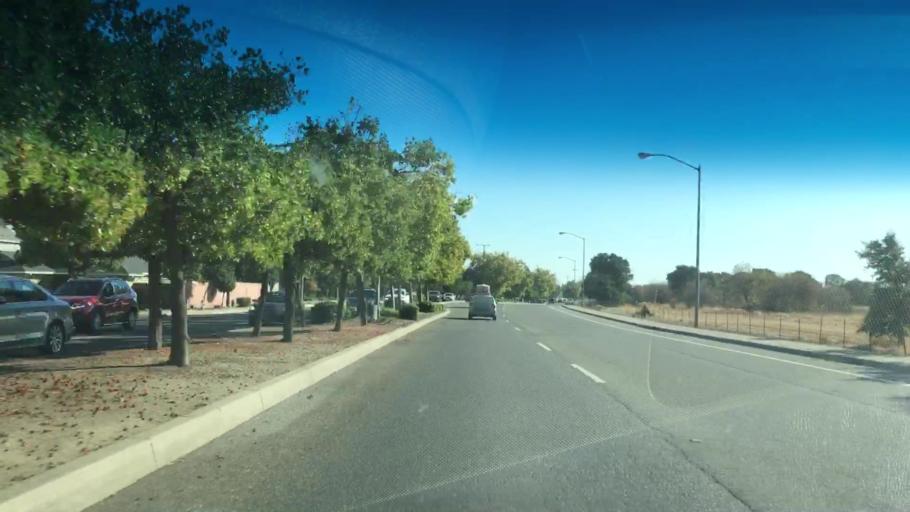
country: US
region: California
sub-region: Sacramento County
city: Laguna
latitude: 38.4524
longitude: -121.4450
